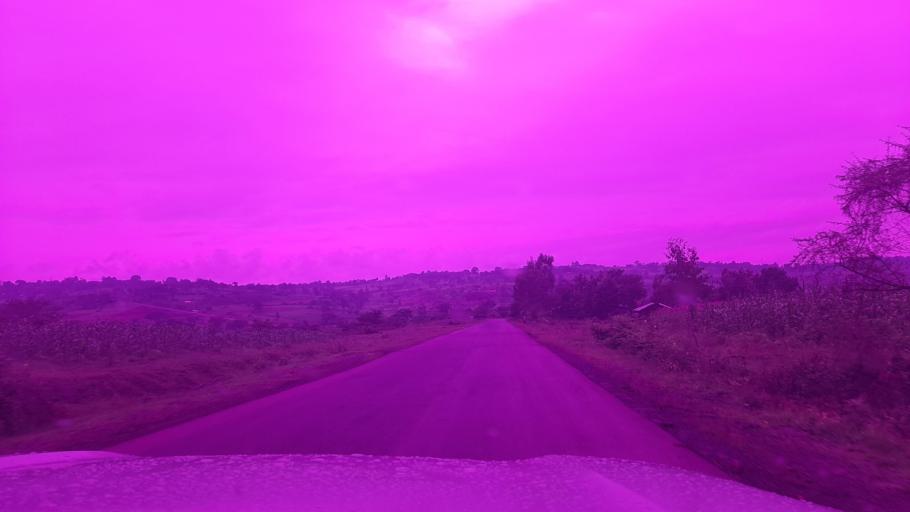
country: ET
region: Oromiya
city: Jima
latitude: 7.7320
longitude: 37.2827
